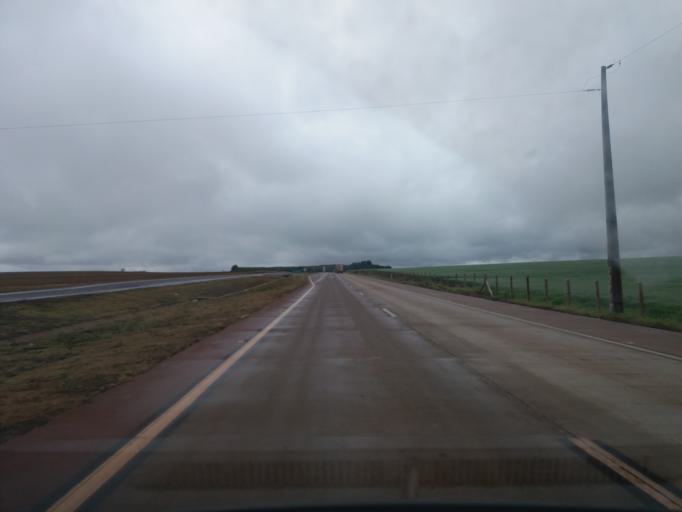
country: BR
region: Parana
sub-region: Cascavel
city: Cascavel
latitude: -25.0726
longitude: -53.5733
